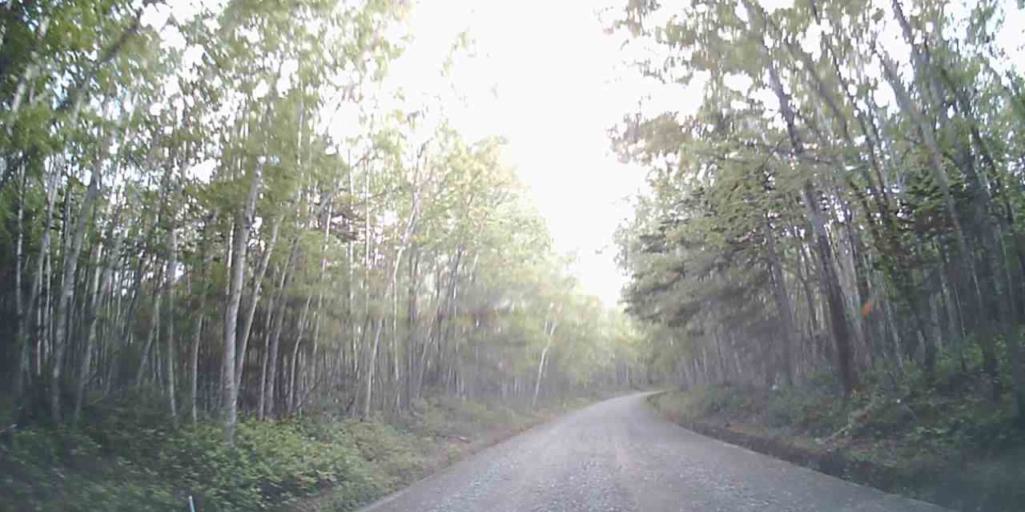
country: JP
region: Hokkaido
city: Shiraoi
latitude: 42.7089
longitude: 141.3982
